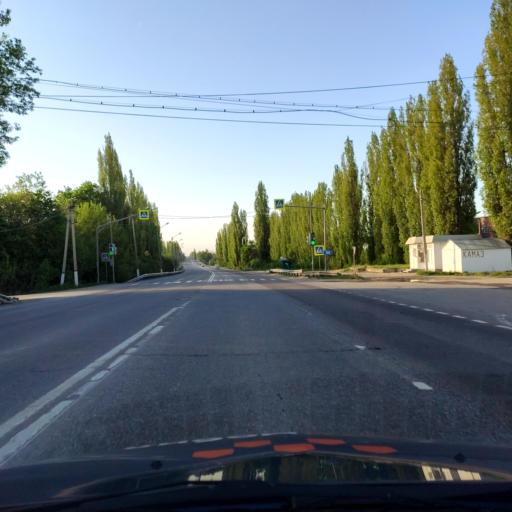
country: RU
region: Lipetsk
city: Yelets
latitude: 52.6089
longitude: 38.4641
